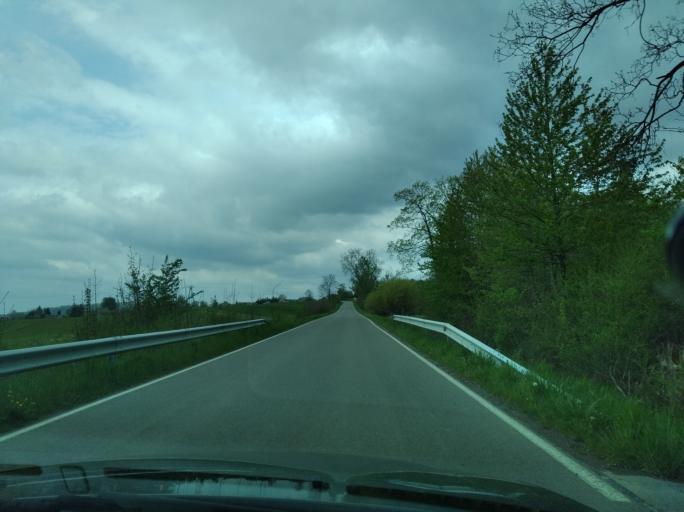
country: PL
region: Subcarpathian Voivodeship
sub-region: Powiat brzozowski
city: Turze Pole
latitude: 49.6348
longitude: 22.0050
